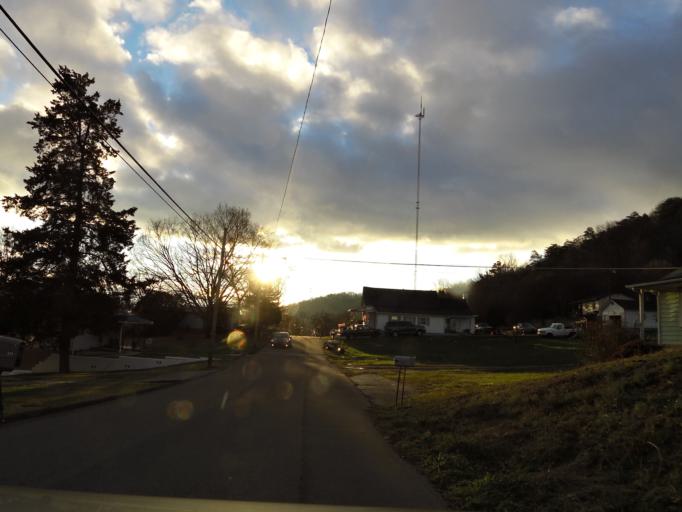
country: US
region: Tennessee
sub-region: Knox County
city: Knoxville
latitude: 35.9981
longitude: -83.9452
